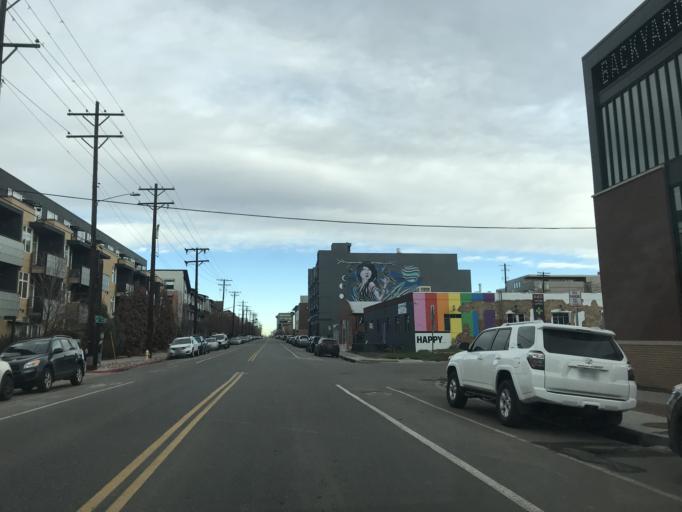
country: US
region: Colorado
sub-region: Denver County
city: Denver
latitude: 39.7643
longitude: -104.9813
